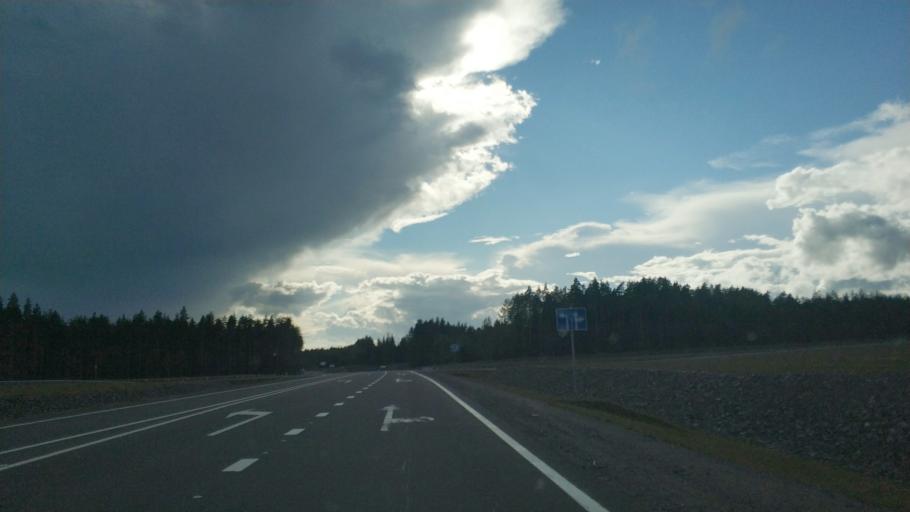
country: RU
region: Republic of Karelia
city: Lakhdenpokh'ya
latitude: 61.5040
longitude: 30.0434
